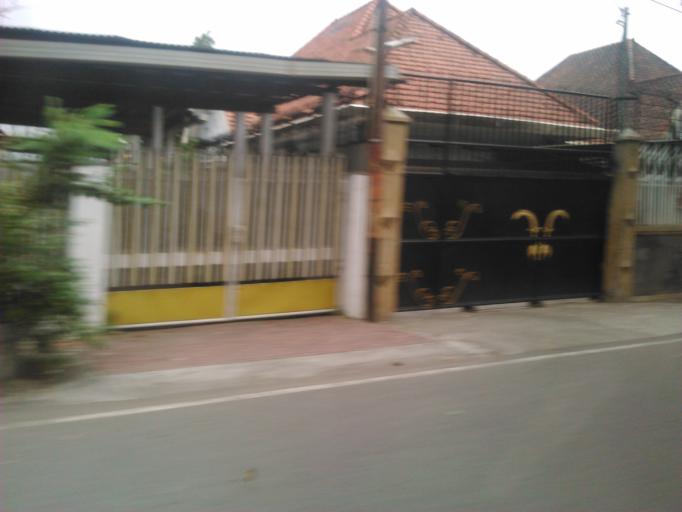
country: ID
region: East Java
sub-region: Kota Surabaya
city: Surabaya
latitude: -7.2579
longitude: 112.7274
